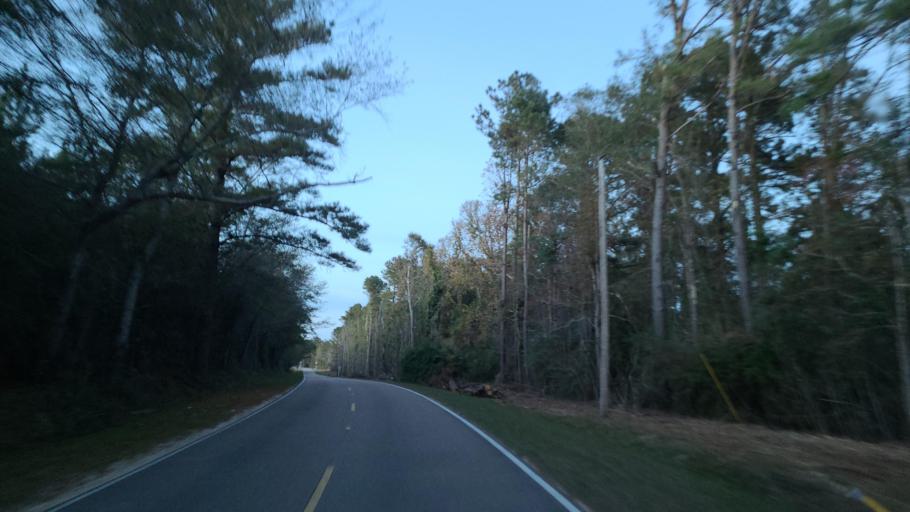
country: US
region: Mississippi
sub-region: Perry County
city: New Augusta
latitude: 31.1289
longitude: -89.1964
